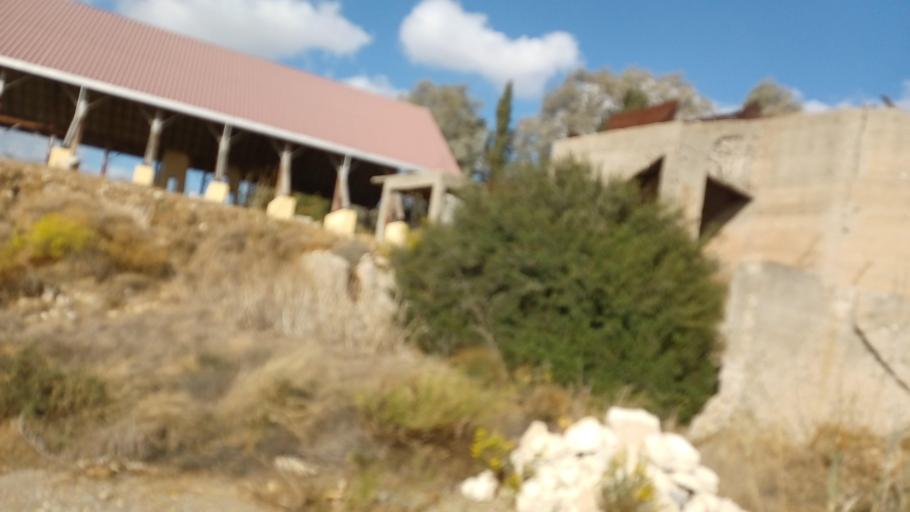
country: CY
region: Limassol
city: Pissouri
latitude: 34.7000
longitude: 32.5541
